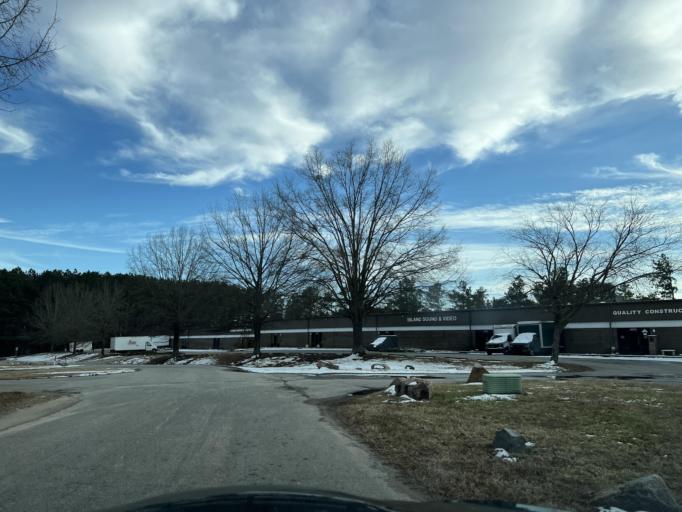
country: US
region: North Carolina
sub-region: Wake County
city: Raleigh
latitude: 35.8666
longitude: -78.5875
